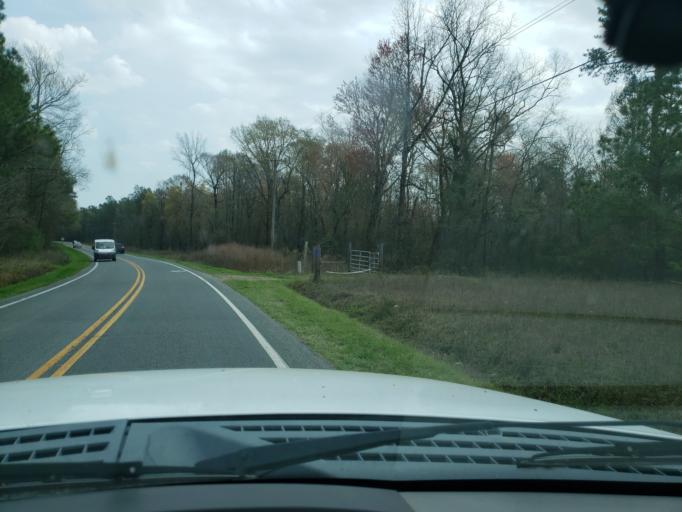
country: US
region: North Carolina
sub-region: Duplin County
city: Wallace
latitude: 34.7900
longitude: -77.8545
